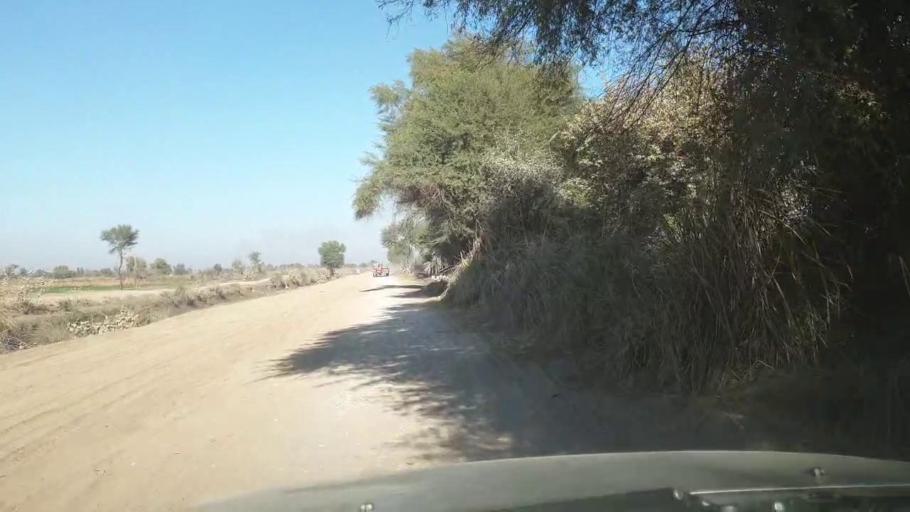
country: PK
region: Sindh
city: Ghotki
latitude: 28.0770
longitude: 69.3465
